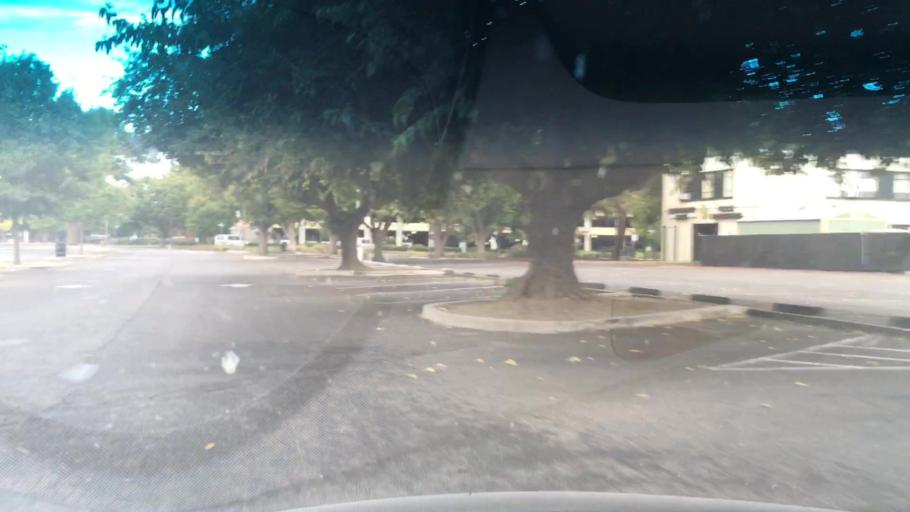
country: US
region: California
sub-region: Sacramento County
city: Rosemont
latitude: 38.5573
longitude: -121.4190
